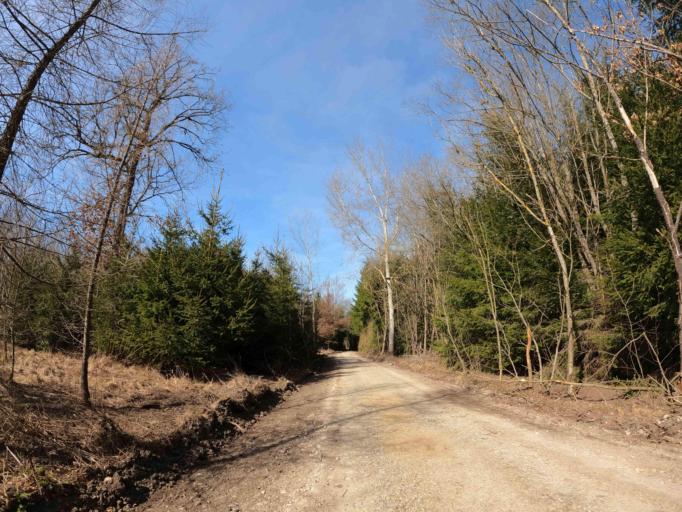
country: DE
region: Bavaria
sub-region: Upper Bavaria
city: Brunnthal
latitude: 47.9947
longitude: 11.7004
